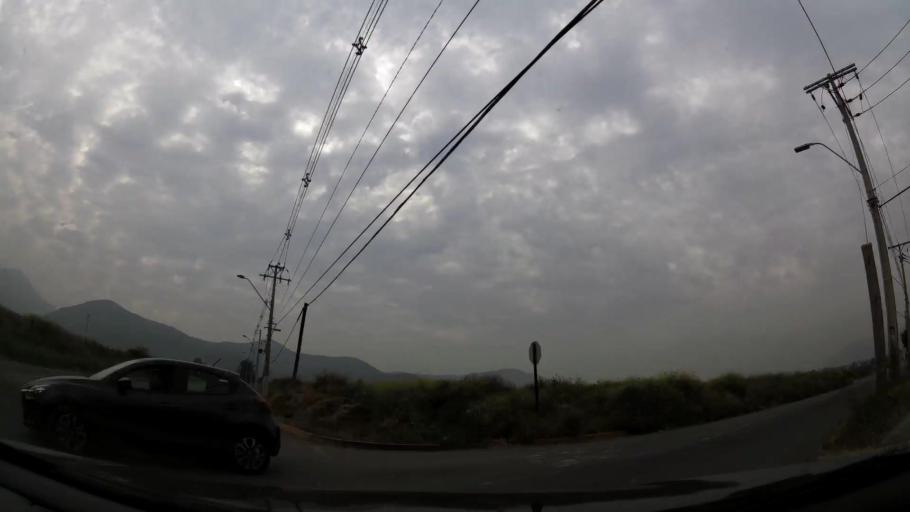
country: CL
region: Santiago Metropolitan
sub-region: Provincia de Chacabuco
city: Chicureo Abajo
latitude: -33.1892
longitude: -70.6766
